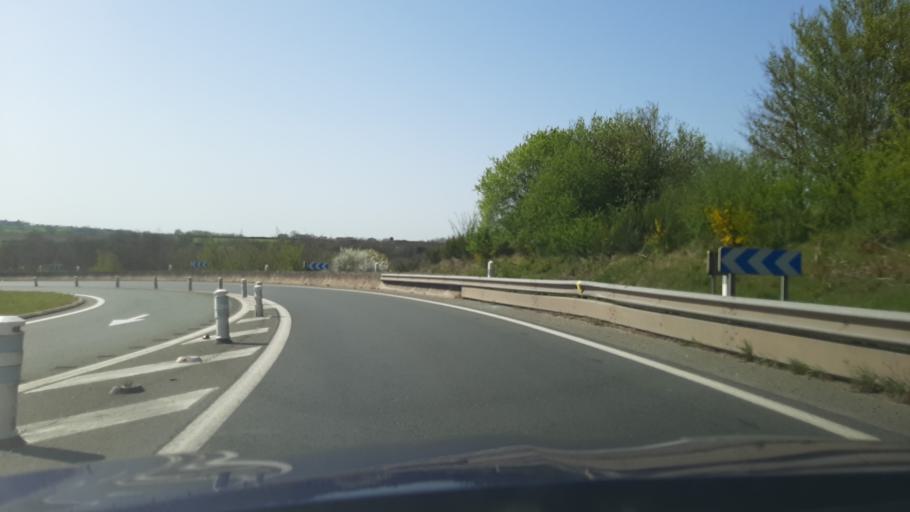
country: FR
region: Pays de la Loire
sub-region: Departement de Maine-et-Loire
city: Murs-Erigne
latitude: 47.3932
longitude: -0.5429
